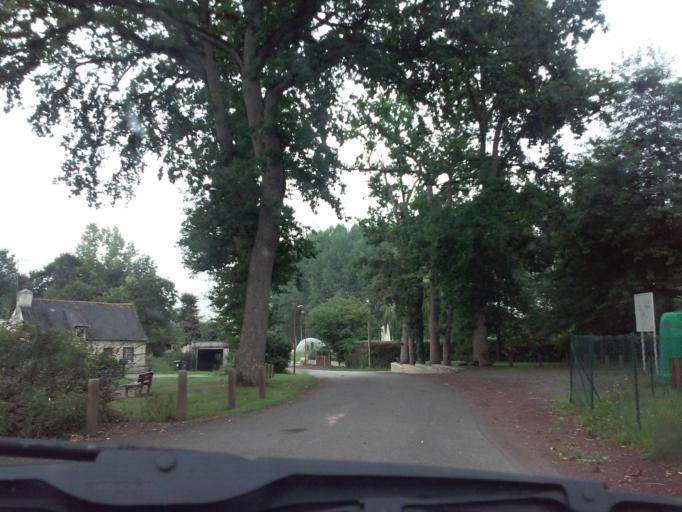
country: FR
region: Brittany
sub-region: Departement du Morbihan
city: Taupont
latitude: 48.0114
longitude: -2.4717
